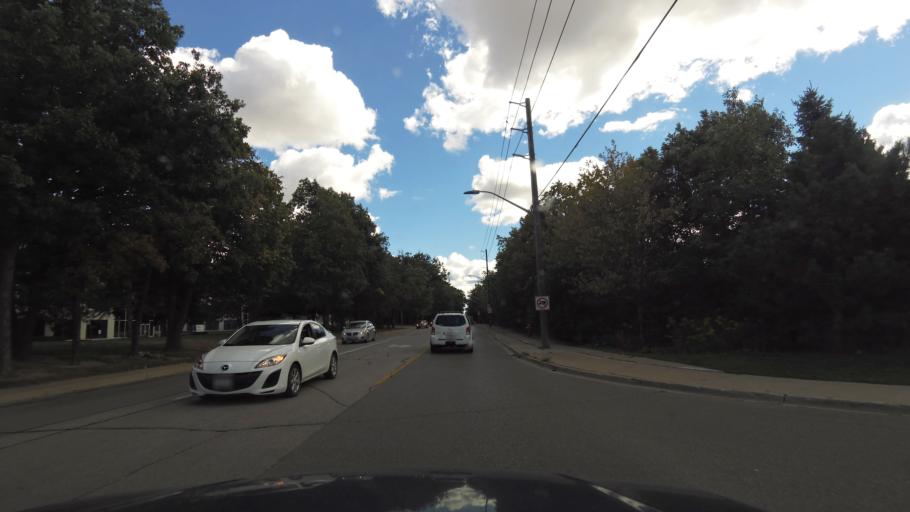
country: CA
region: Ontario
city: Mississauga
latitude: 43.6105
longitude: -79.6817
